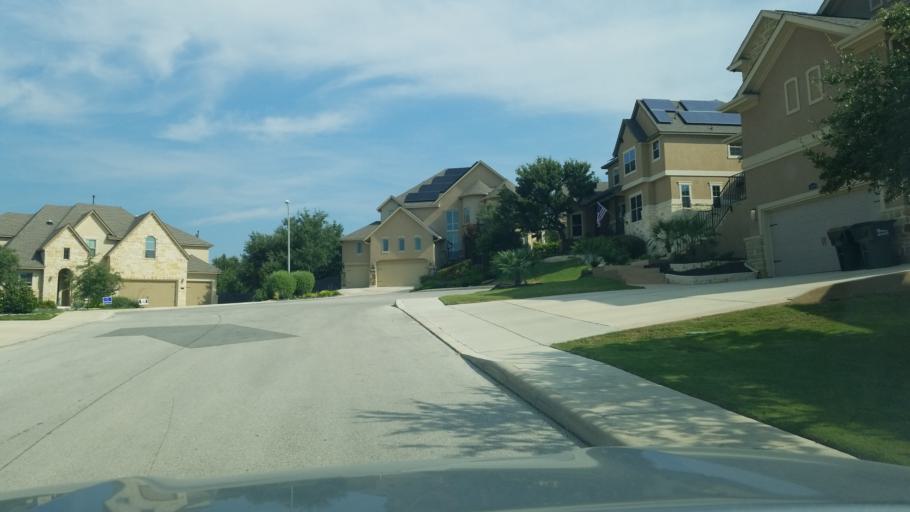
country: US
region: Texas
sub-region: Bexar County
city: Scenic Oaks
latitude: 29.7168
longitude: -98.6574
